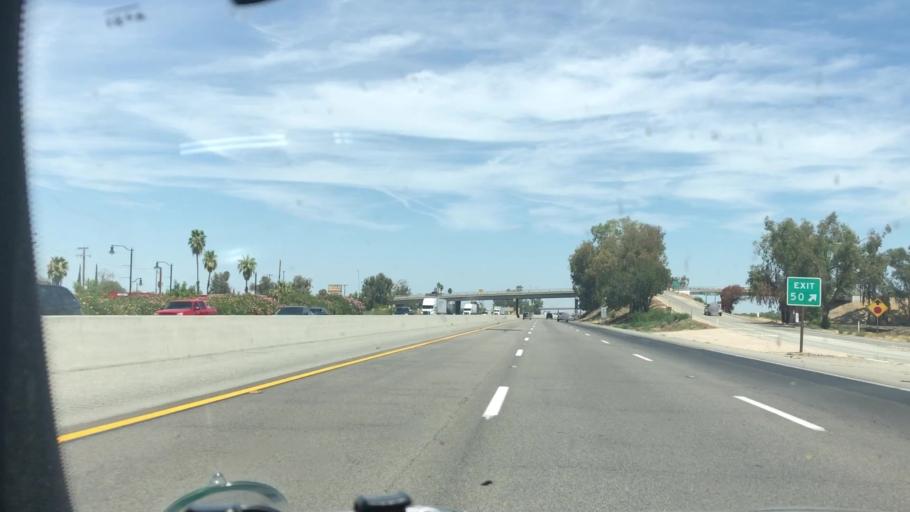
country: US
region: California
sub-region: Kern County
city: McFarland
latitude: 35.6804
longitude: -119.2280
